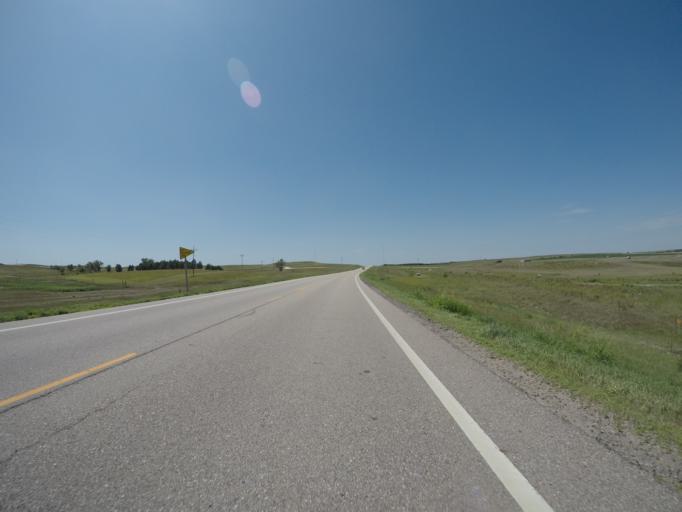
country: US
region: Kansas
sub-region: Osborne County
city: Osborne
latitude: 39.4988
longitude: -98.6938
